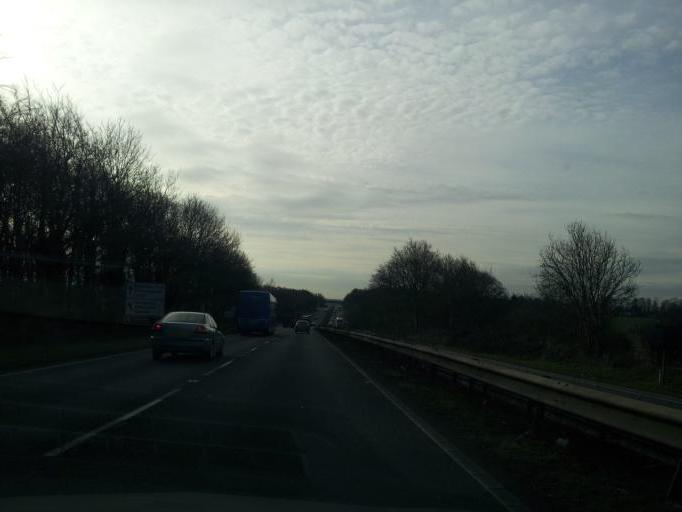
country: GB
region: England
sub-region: Peterborough
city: Thornhaugh
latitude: 52.5914
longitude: -0.4172
